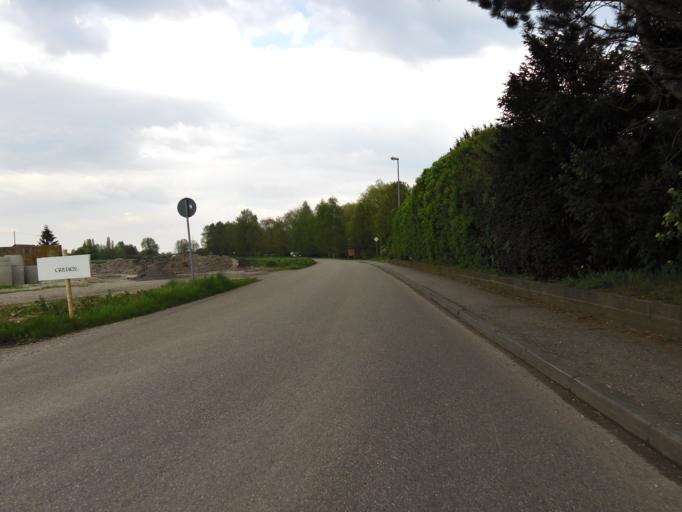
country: DE
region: Bavaria
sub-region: Upper Bavaria
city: Eitting
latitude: 48.3646
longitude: 11.8954
